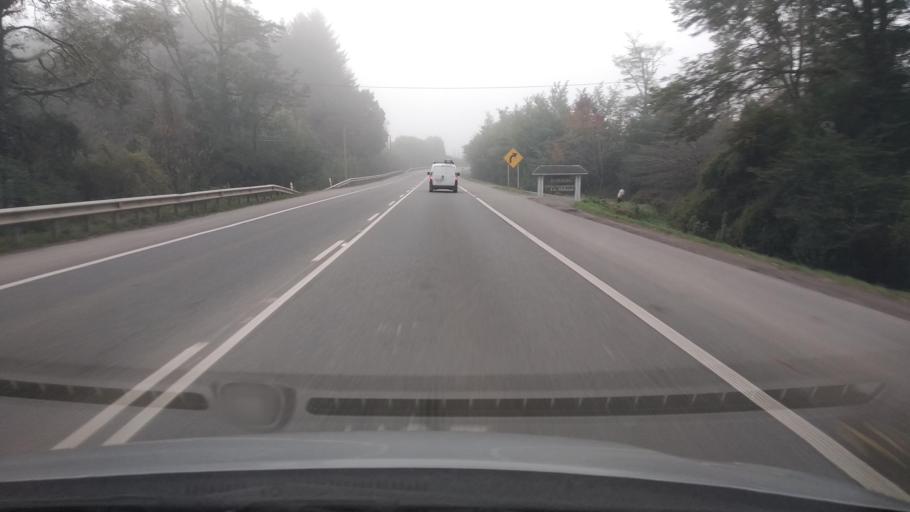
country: CL
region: Los Lagos
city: Las Animas
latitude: -39.7528
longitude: -73.2289
